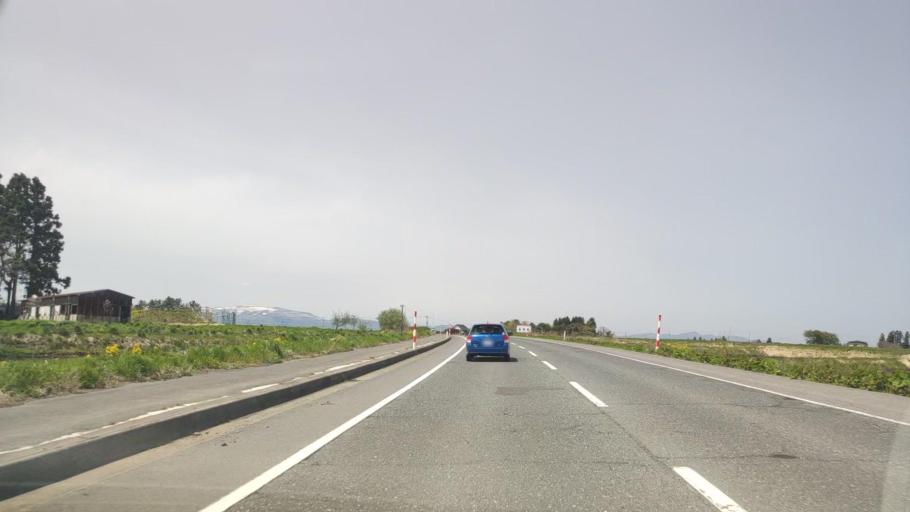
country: JP
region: Aomori
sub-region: Misawa Shi
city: Inuotose
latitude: 40.6370
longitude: 141.2416
